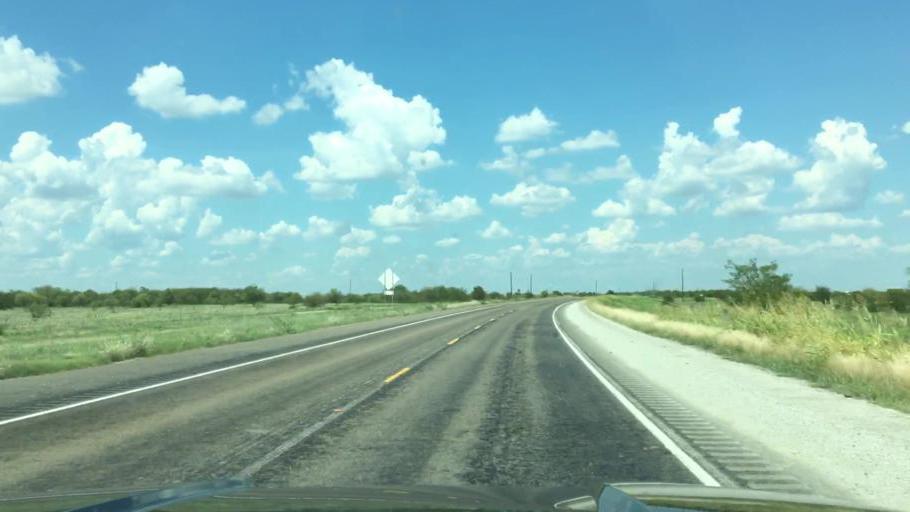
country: US
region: Texas
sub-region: Tarrant County
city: Haslet
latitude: 33.0058
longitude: -97.3420
